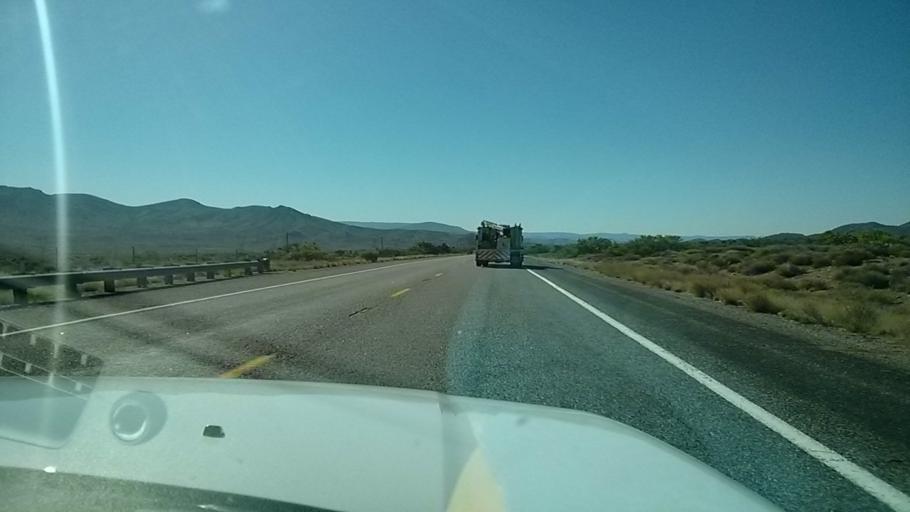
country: US
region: Arizona
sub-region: Mohave County
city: New Kingman-Butler
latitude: 35.4070
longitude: -113.7710
